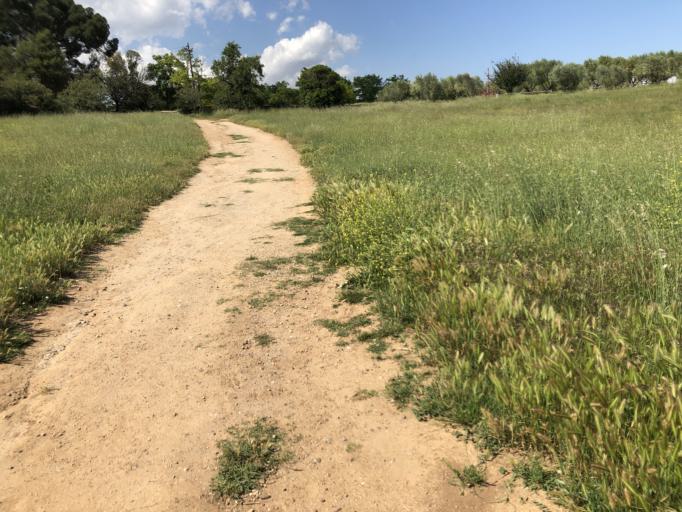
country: ES
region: Catalonia
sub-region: Provincia de Barcelona
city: Rubi
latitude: 41.4919
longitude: 2.0415
